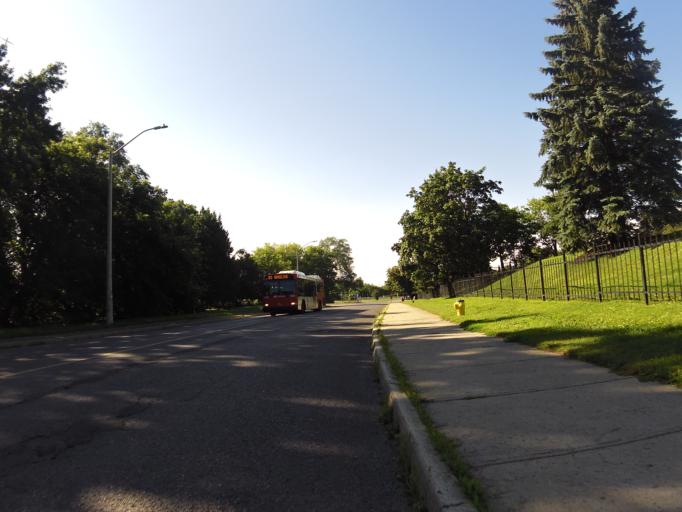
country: CA
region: Ontario
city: Ottawa
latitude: 45.3462
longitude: -75.7267
